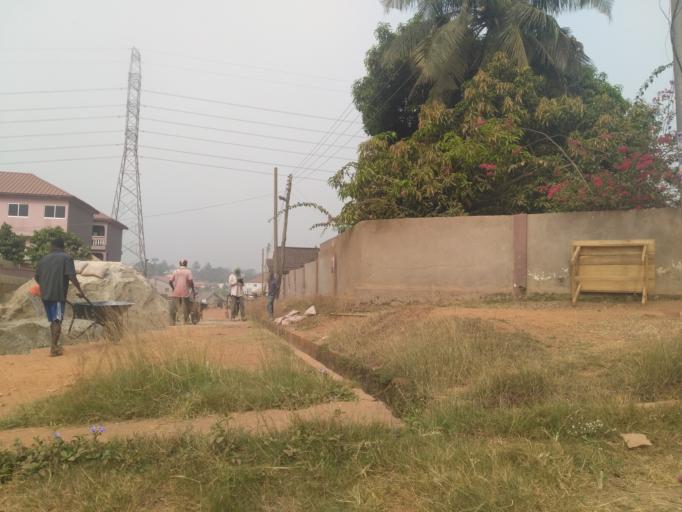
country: GH
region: Ashanti
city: Kumasi
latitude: 6.6608
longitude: -1.6143
